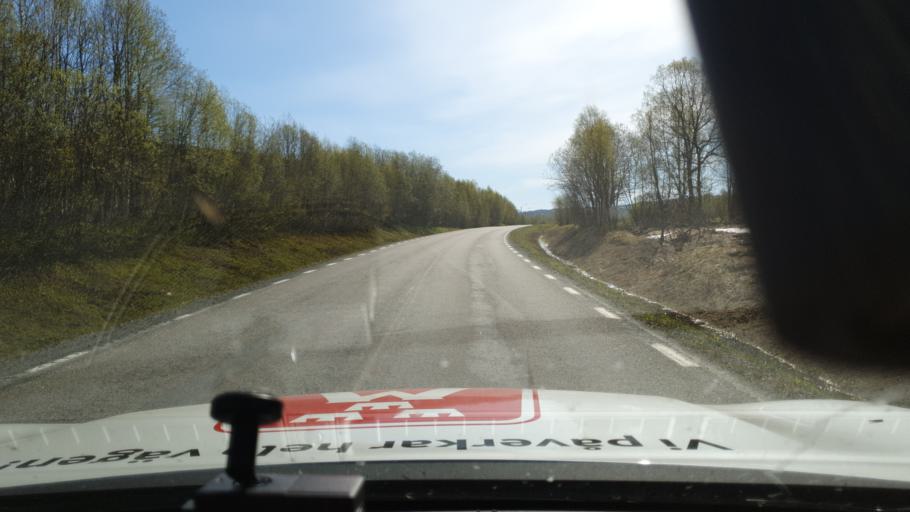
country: NO
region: Nordland
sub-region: Hattfjelldal
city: Hattfjelldal
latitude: 65.7532
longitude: 14.9539
